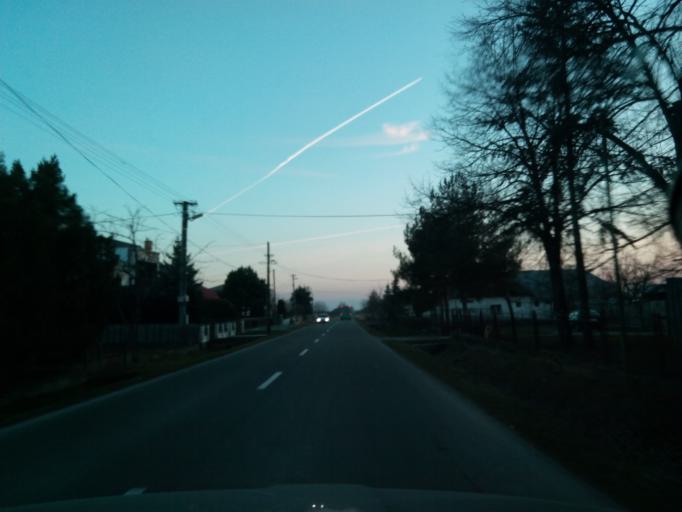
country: SK
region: Kosicky
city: Sobrance
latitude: 48.7849
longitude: 22.1316
